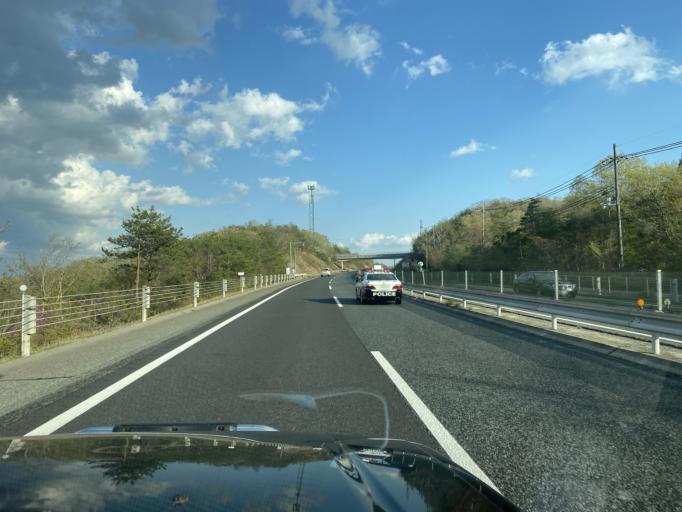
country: JP
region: Hyogo
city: Sandacho
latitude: 34.9544
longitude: 135.1369
